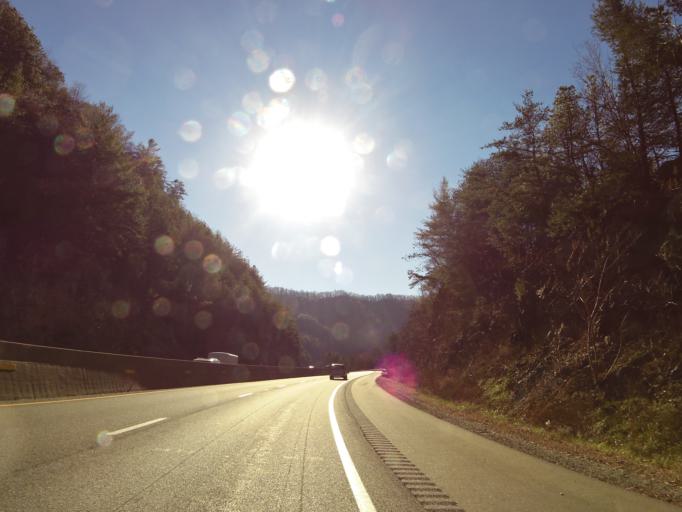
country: US
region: North Carolina
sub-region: Haywood County
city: Cove Creek
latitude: 35.7159
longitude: -83.0333
